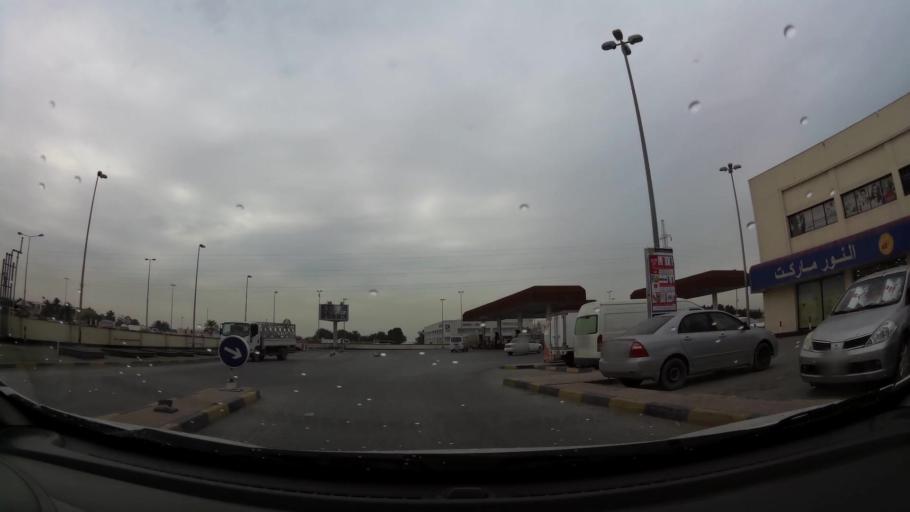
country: BH
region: Northern
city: Sitrah
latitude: 26.1651
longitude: 50.6060
